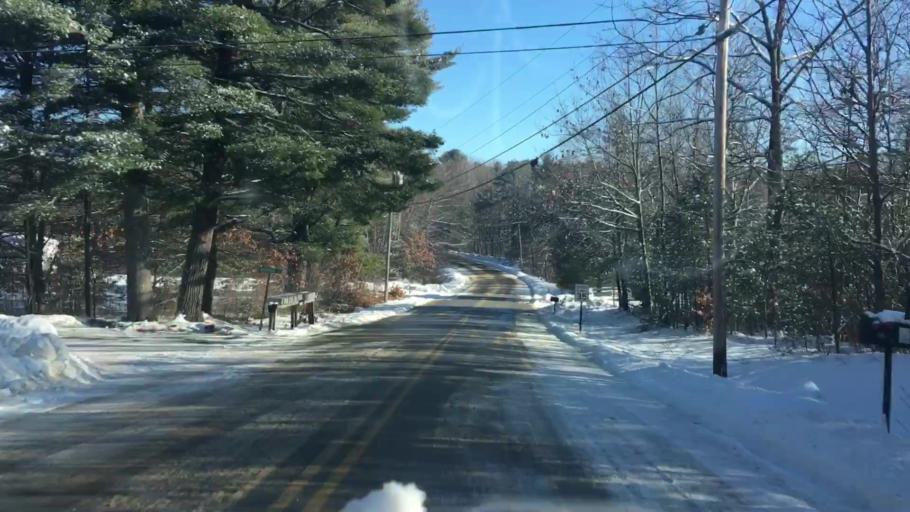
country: US
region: Maine
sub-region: Cumberland County
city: New Gloucester
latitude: 43.9578
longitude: -70.3266
